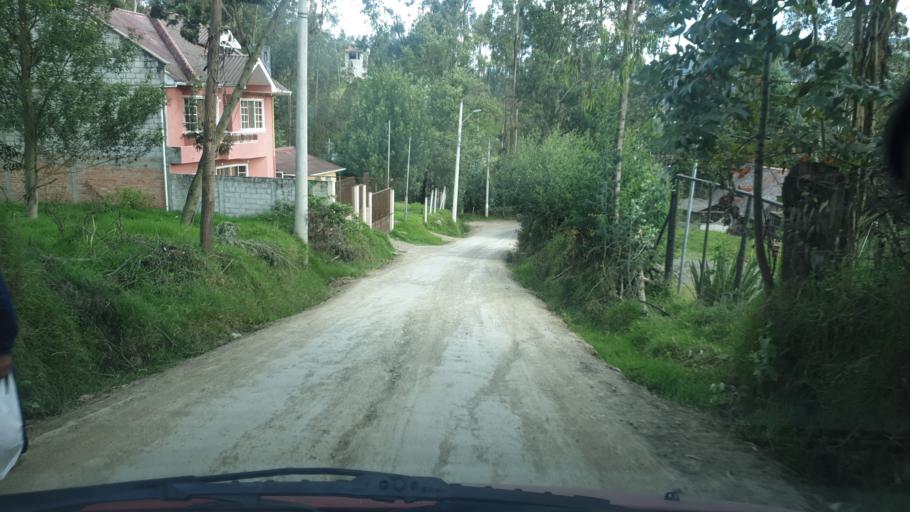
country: EC
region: Azuay
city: Cuenca
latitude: -2.9187
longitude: -78.9777
